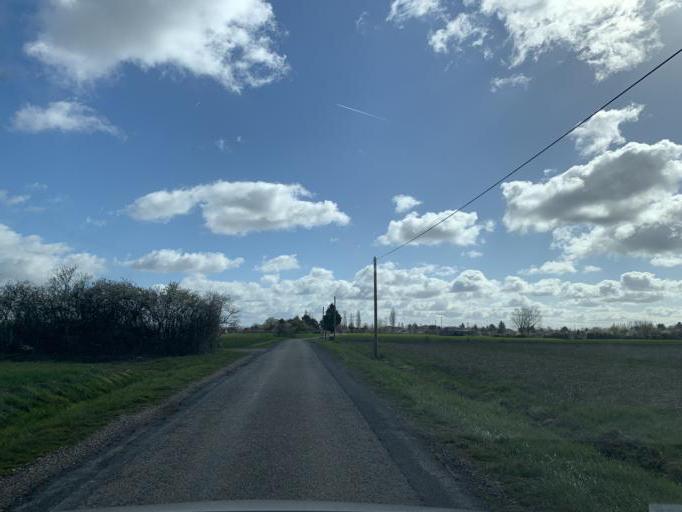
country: FR
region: Rhone-Alpes
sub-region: Departement de l'Ain
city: Saint-Andre-de-Corcy
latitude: 45.9507
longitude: 4.9738
